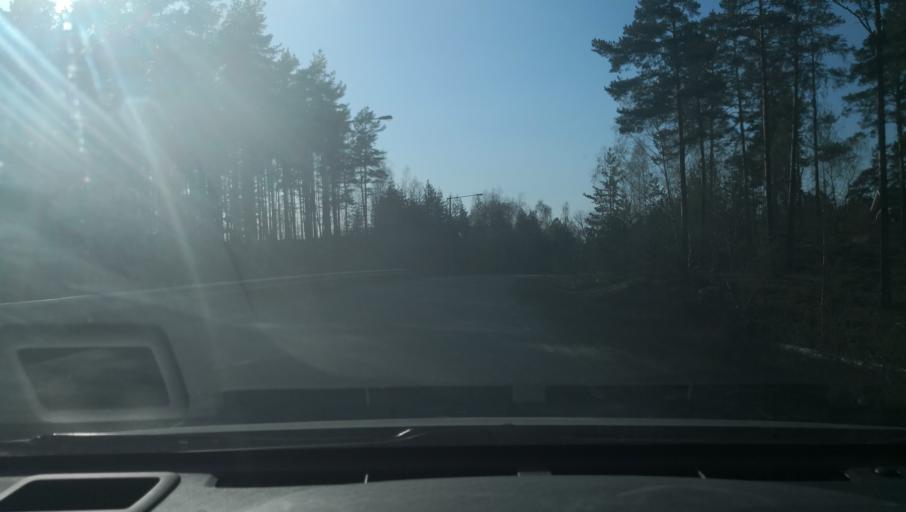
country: SE
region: Uppsala
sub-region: Heby Kommun
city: Tarnsjo
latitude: 60.1545
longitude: 16.9343
